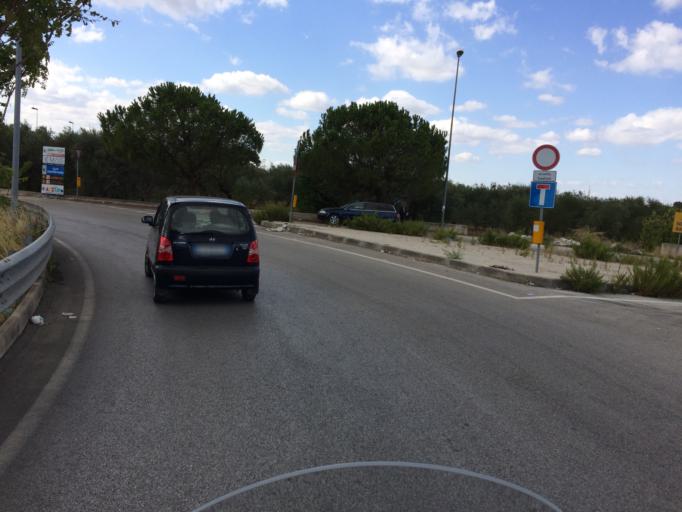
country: IT
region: Apulia
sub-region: Provincia di Bari
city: Modugno
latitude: 41.0945
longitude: 16.8277
